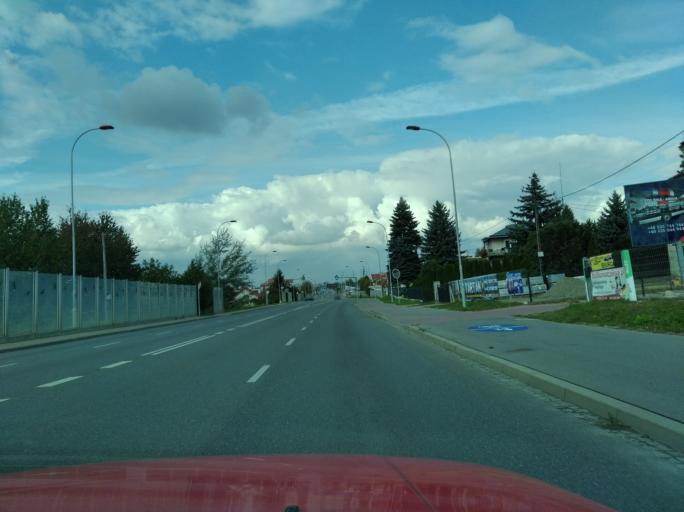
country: PL
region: Subcarpathian Voivodeship
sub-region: Powiat rzeszowski
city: Tyczyn
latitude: 49.9959
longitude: 22.0181
